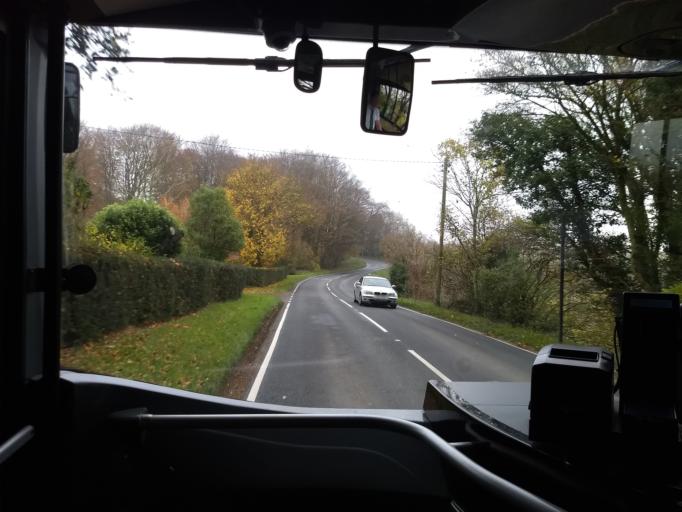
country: GB
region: England
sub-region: Isle of Wight
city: Newchurch
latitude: 50.6810
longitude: -1.2487
